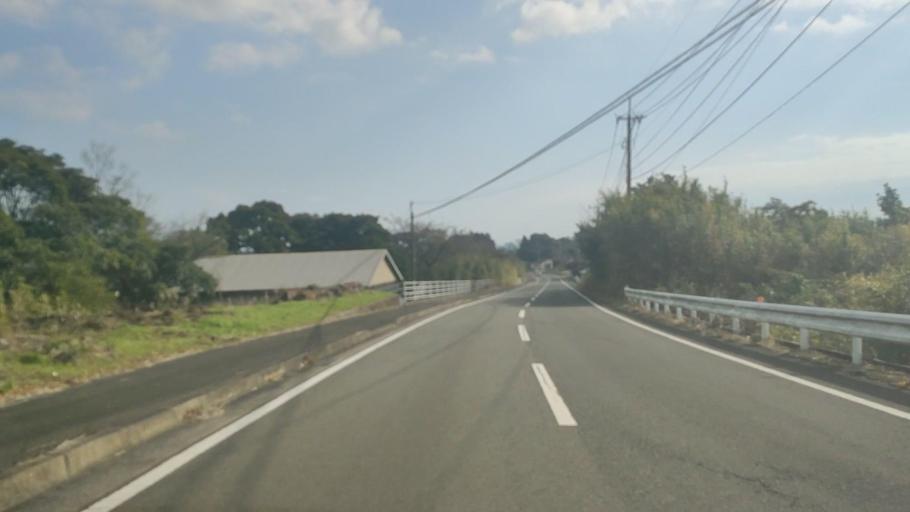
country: JP
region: Nagasaki
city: Shimabara
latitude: 32.6819
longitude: 130.2757
